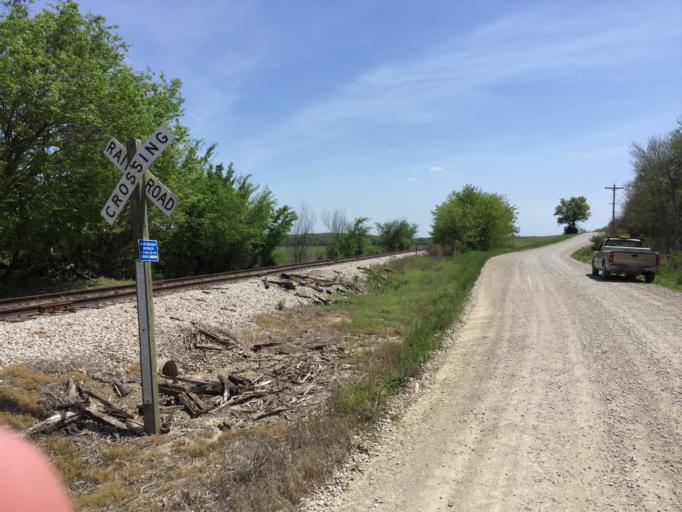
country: US
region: Kansas
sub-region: Montgomery County
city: Cherryvale
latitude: 37.3188
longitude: -95.5849
